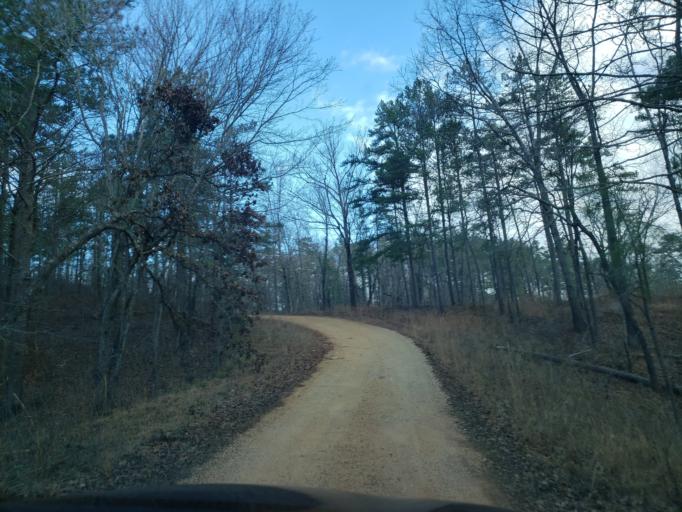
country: US
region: Alabama
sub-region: Cleburne County
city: Heflin
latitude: 33.6891
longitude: -85.6361
